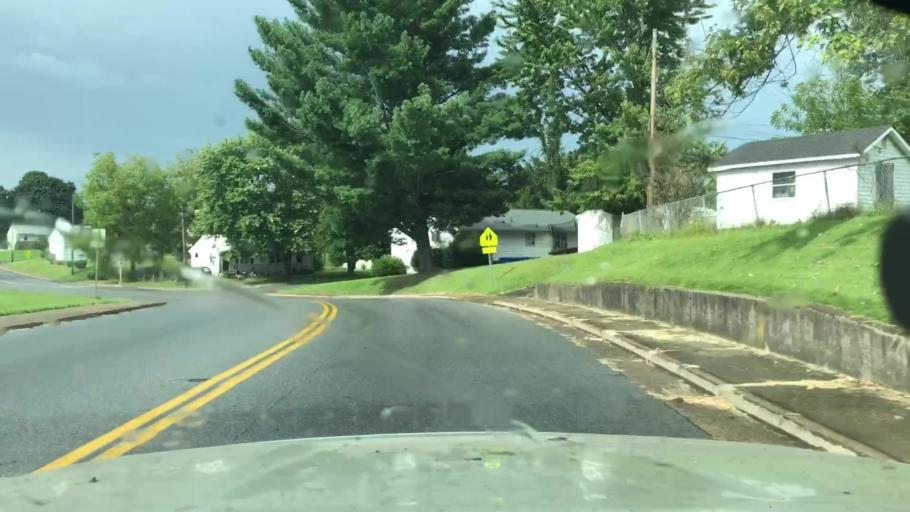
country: US
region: Virginia
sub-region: City of Waynesboro
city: Waynesboro
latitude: 38.0778
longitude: -78.8951
